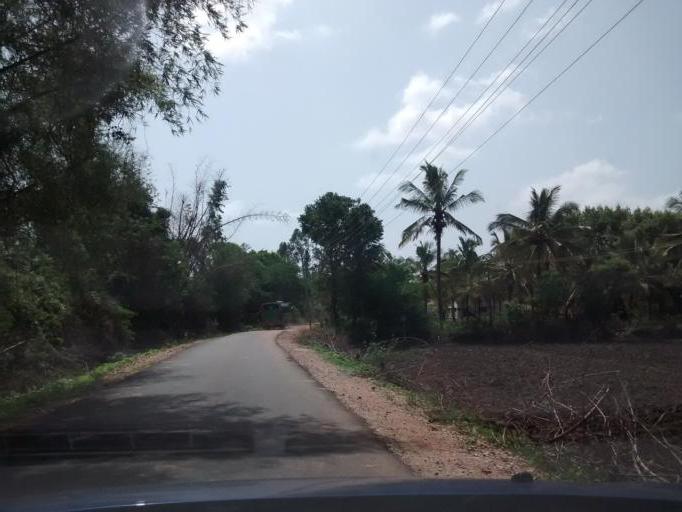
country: IN
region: Karnataka
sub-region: Hassan
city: Hole Narsipur
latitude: 12.6972
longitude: 76.1693
